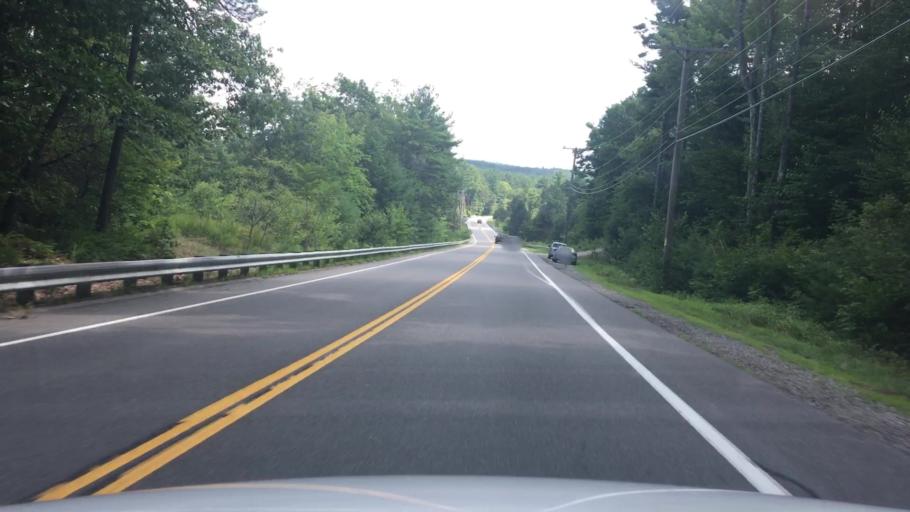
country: US
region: New Hampshire
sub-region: Rockingham County
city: Auburn
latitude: 42.9903
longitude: -71.3779
